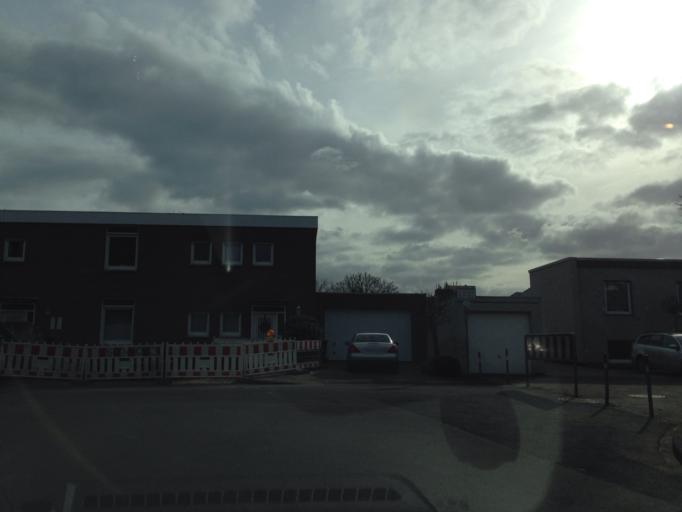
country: DE
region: North Rhine-Westphalia
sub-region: Regierungsbezirk Munster
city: Muenster
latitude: 52.0003
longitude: 7.5994
